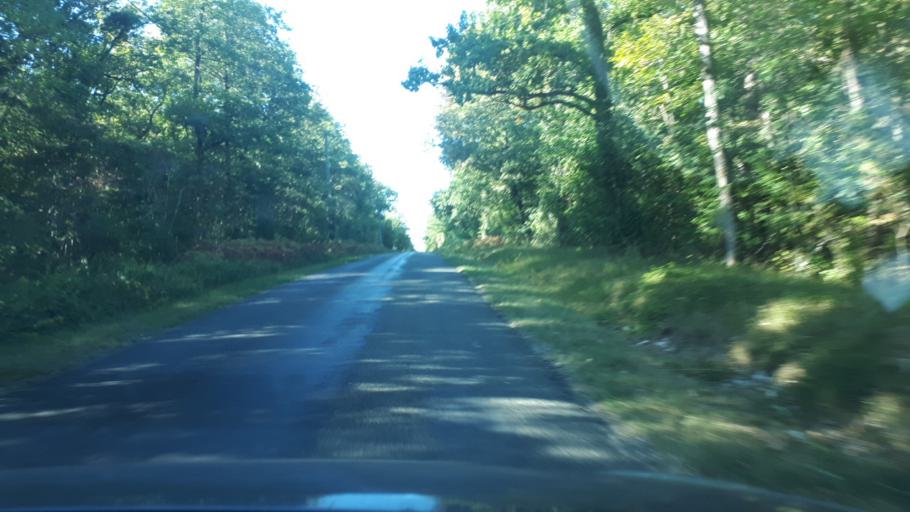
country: FR
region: Centre
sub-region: Departement du Cher
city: Sancerre
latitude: 47.2686
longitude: 2.7546
